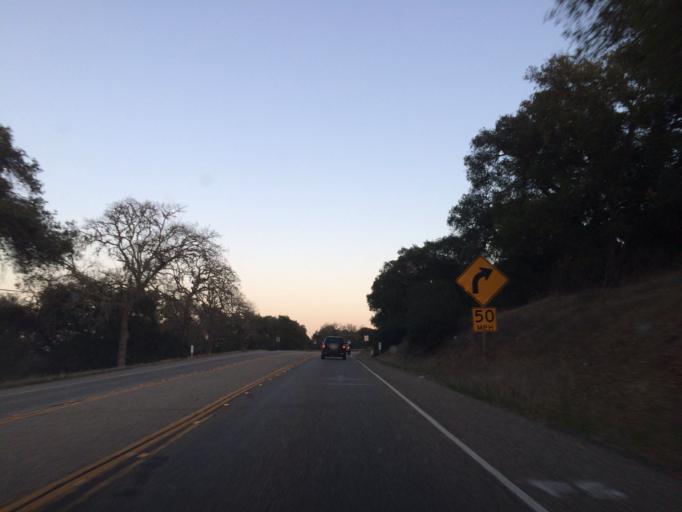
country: US
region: California
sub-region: Santa Barbara County
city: Santa Ynez
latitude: 34.5852
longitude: -119.9963
